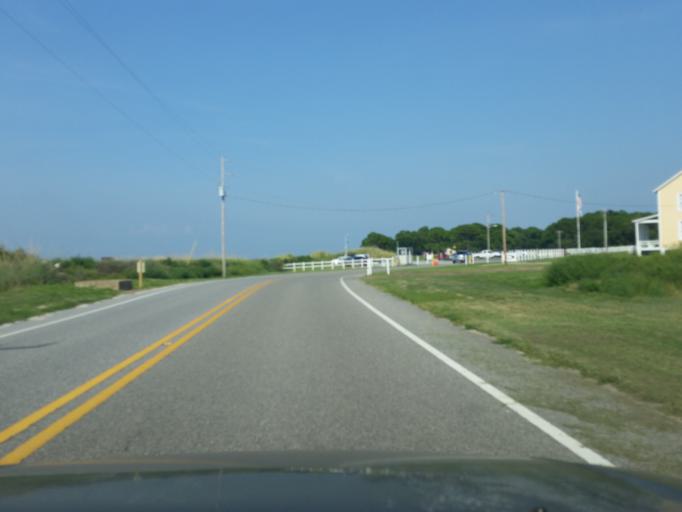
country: US
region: Alabama
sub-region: Mobile County
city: Dauphin Island
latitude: 30.2310
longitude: -88.0196
